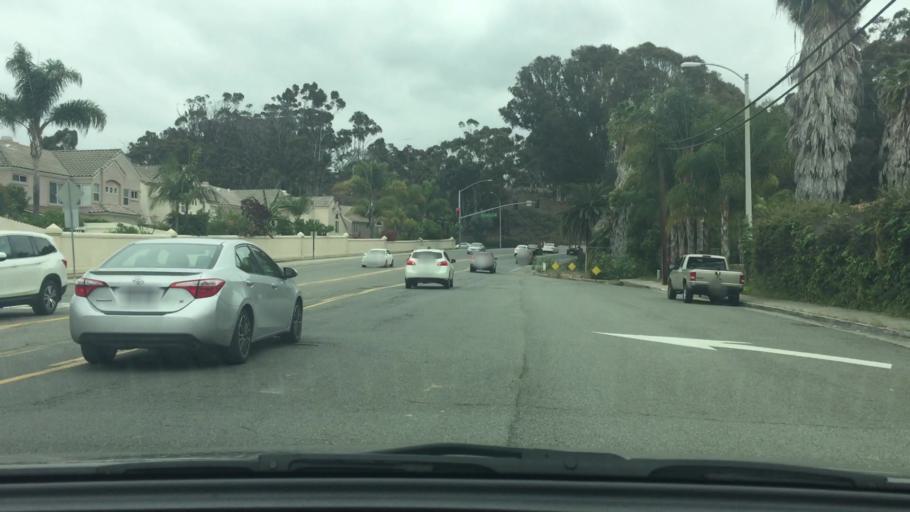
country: US
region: California
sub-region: San Diego County
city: Bonita
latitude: 32.6591
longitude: -117.0570
